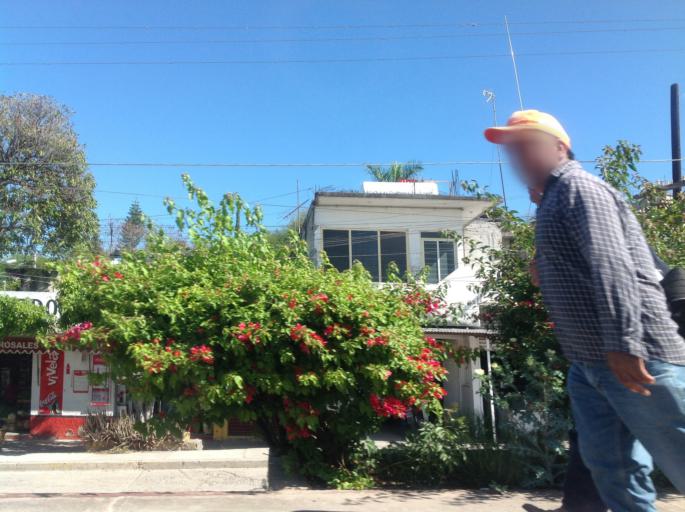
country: MX
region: Oaxaca
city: Ciudad de Huajuapam de Leon
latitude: 17.8139
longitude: -97.7639
